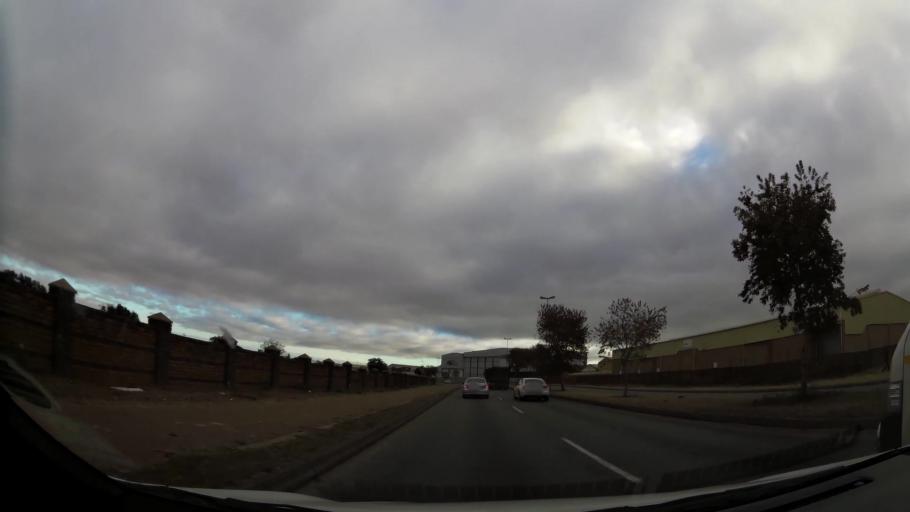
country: ZA
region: Limpopo
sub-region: Capricorn District Municipality
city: Polokwane
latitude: -23.8948
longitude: 29.4377
